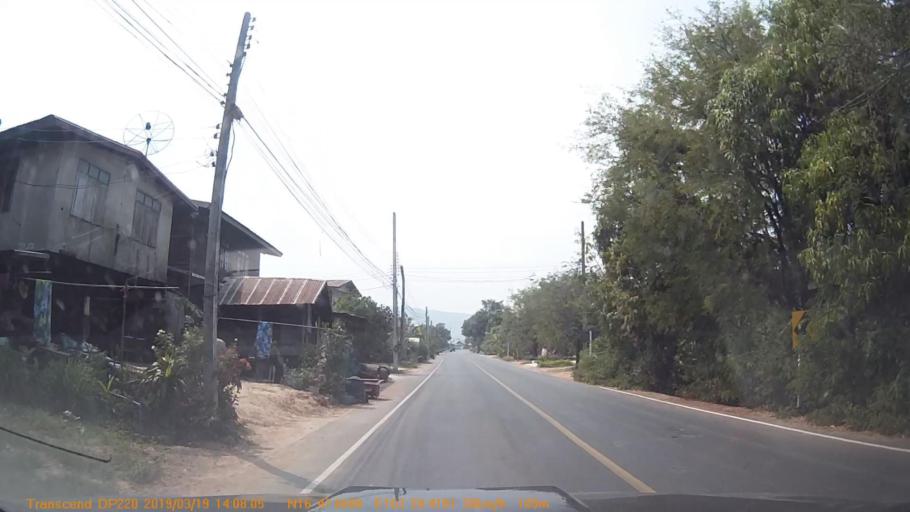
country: TH
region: Kalasin
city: Na Khu
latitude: 16.7946
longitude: 103.9899
